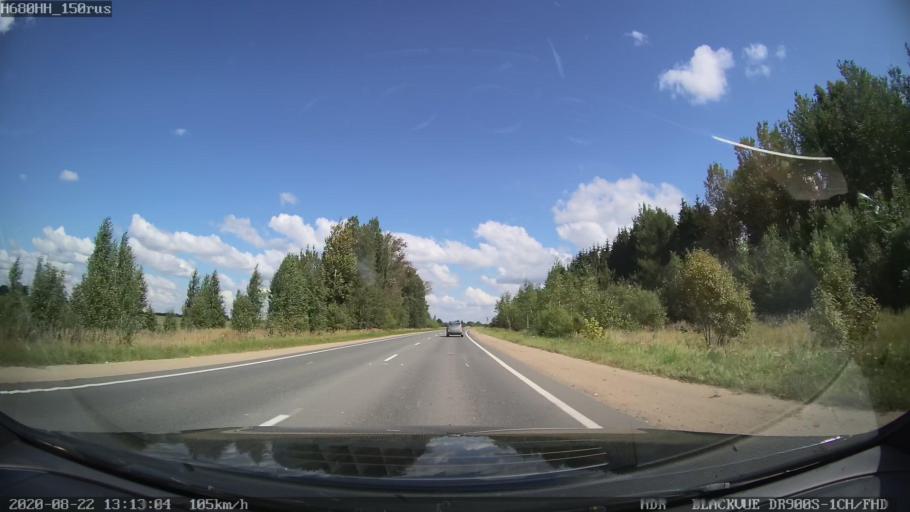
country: RU
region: Tverskaya
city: Bezhetsk
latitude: 57.7475
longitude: 36.5624
